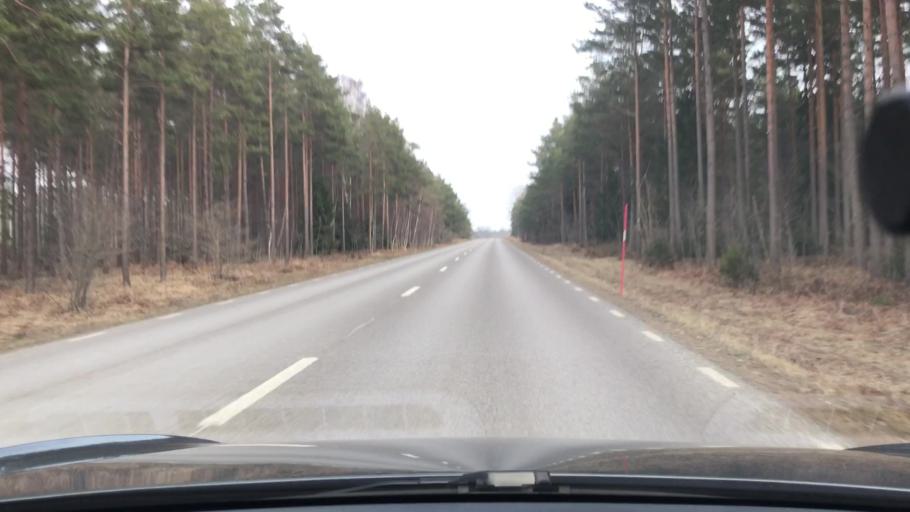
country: SE
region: Gotland
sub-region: Gotland
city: Slite
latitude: 57.4357
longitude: 18.6705
